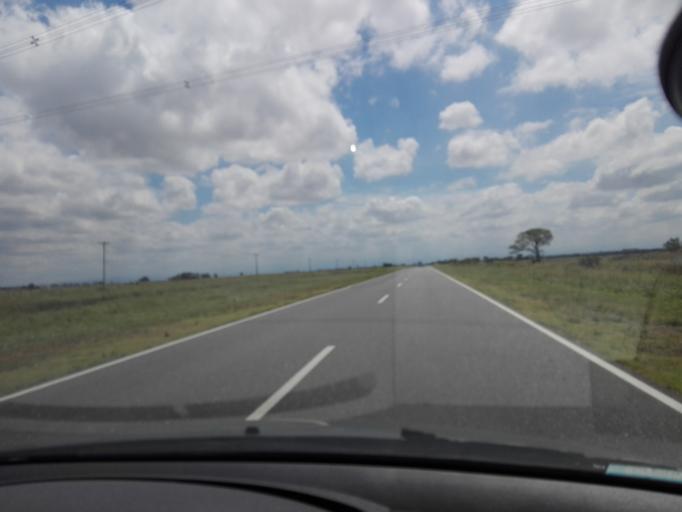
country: AR
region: Cordoba
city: Toledo
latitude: -31.6461
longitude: -64.0383
